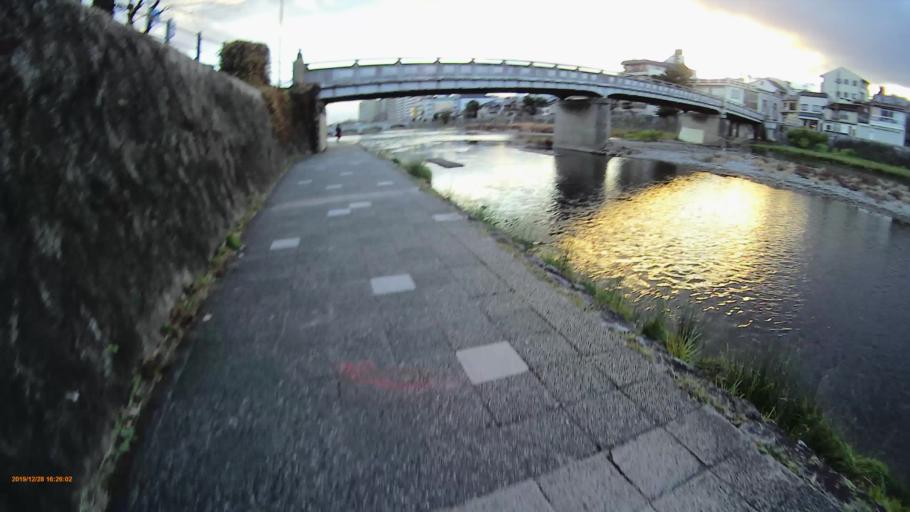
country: JP
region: Kyoto
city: Kyoto
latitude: 34.9911
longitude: 135.7677
